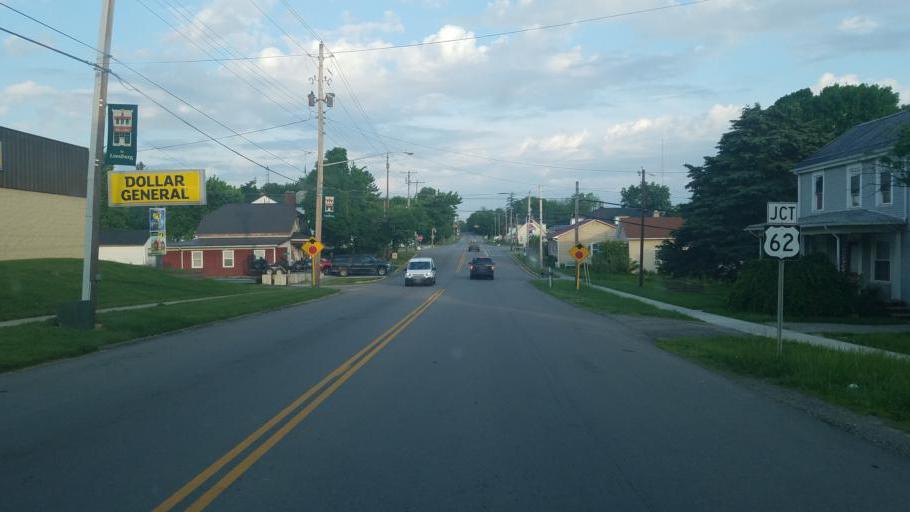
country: US
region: Ohio
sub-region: Highland County
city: Leesburg
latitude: 39.3455
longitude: -83.5580
